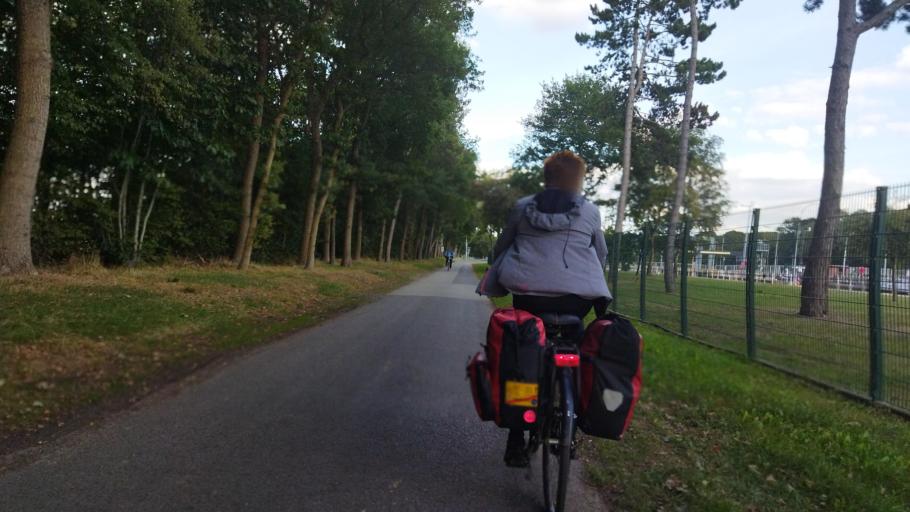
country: DE
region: Lower Saxony
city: Heede
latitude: 52.9847
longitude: 7.3125
